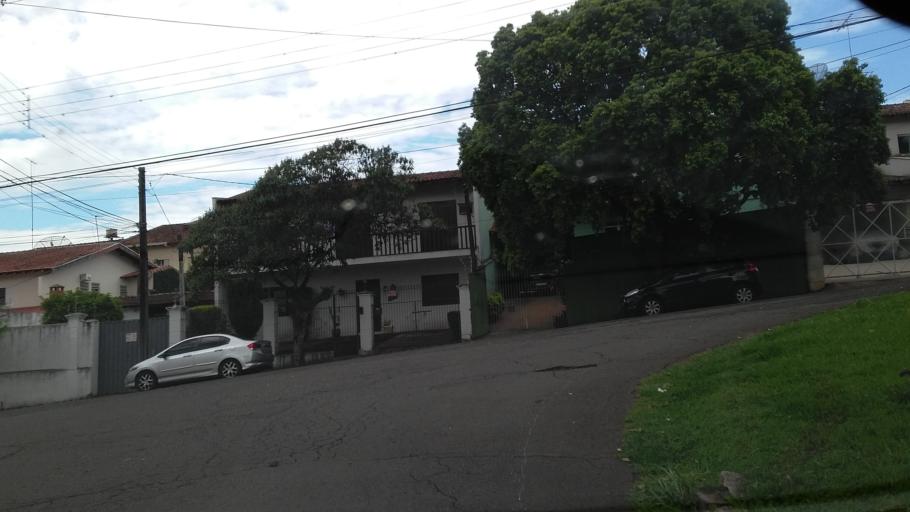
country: BR
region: Parana
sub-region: Londrina
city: Londrina
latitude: -23.3246
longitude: -51.1753
